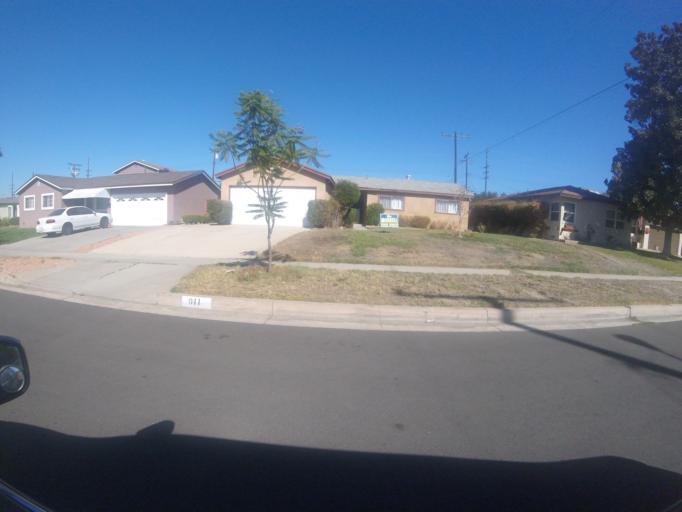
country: US
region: California
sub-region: San Bernardino County
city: Redlands
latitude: 34.0692
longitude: -117.1709
